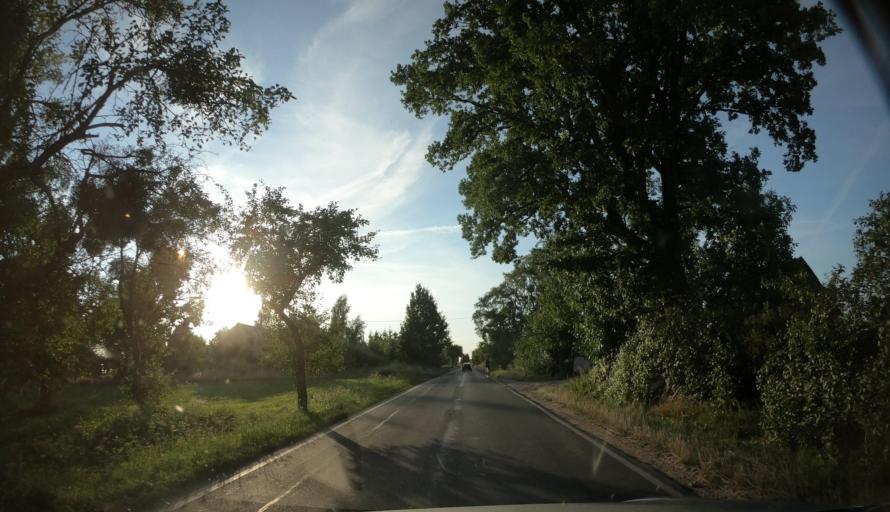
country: PL
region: Kujawsko-Pomorskie
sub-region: Powiat swiecki
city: Pruszcz
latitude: 53.2504
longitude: 18.1937
